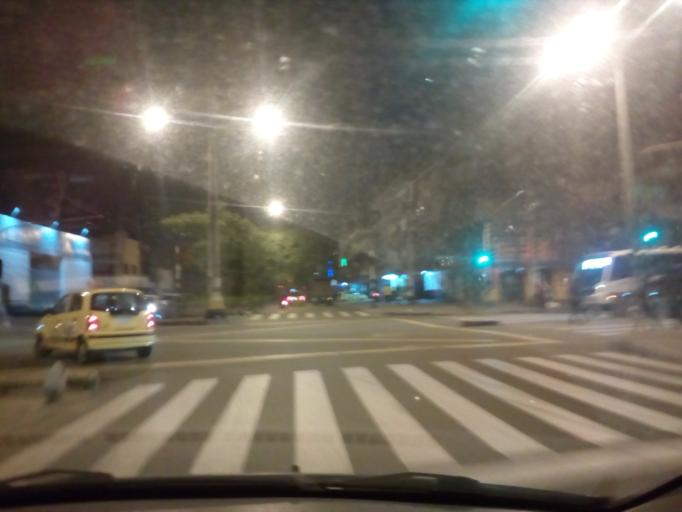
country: CO
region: Antioquia
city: Itagui
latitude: 6.1916
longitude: -75.5925
